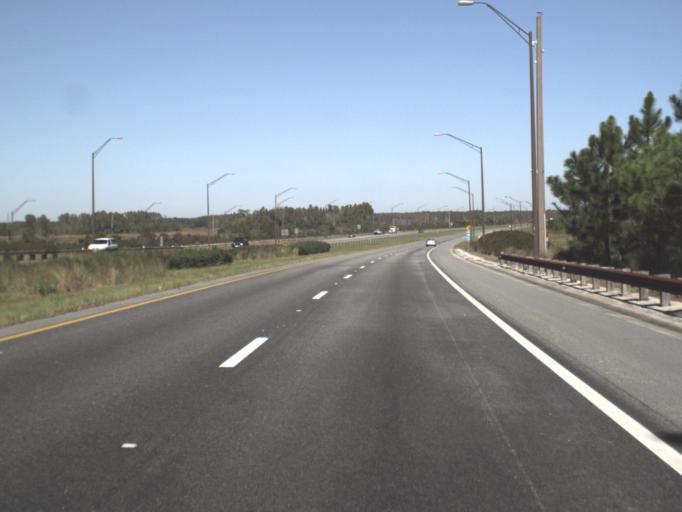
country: US
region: Florida
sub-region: Pasco County
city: Odessa
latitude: 28.1920
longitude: -82.5452
